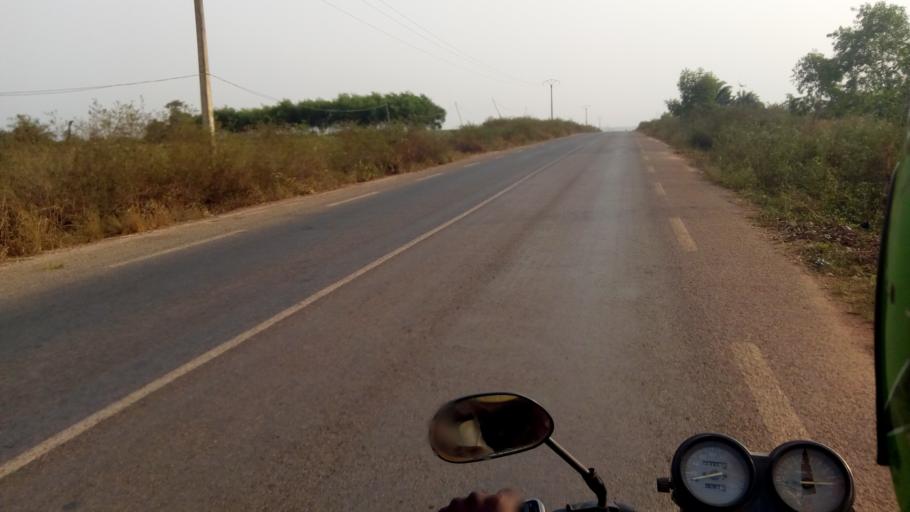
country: BJ
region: Atlantique
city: Hinvi
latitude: 6.7065
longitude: 2.2907
